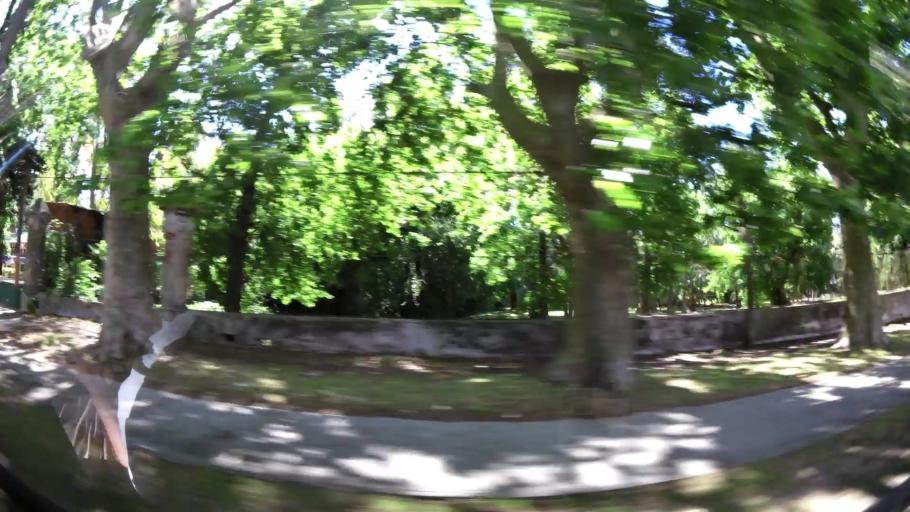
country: UY
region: Montevideo
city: Montevideo
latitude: -34.8426
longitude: -56.1989
